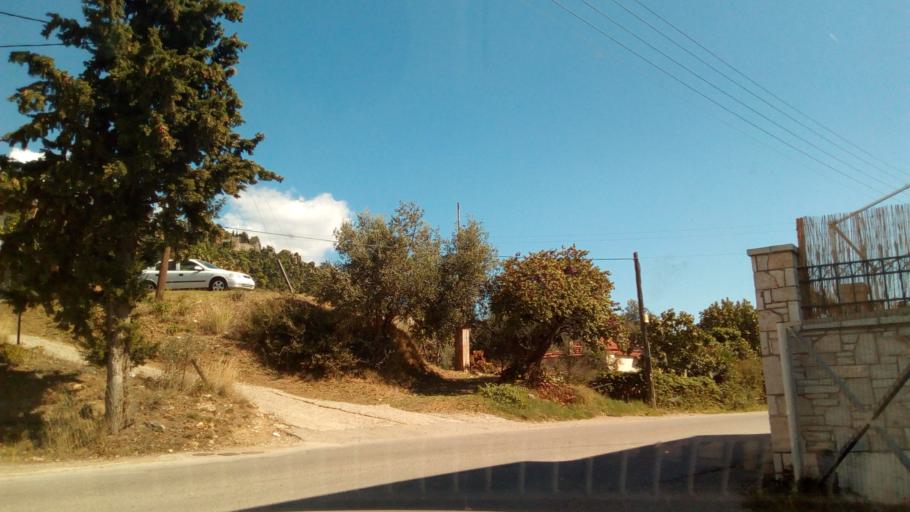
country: GR
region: West Greece
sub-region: Nomos Aitolias kai Akarnanias
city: Nafpaktos
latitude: 38.3927
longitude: 21.8172
